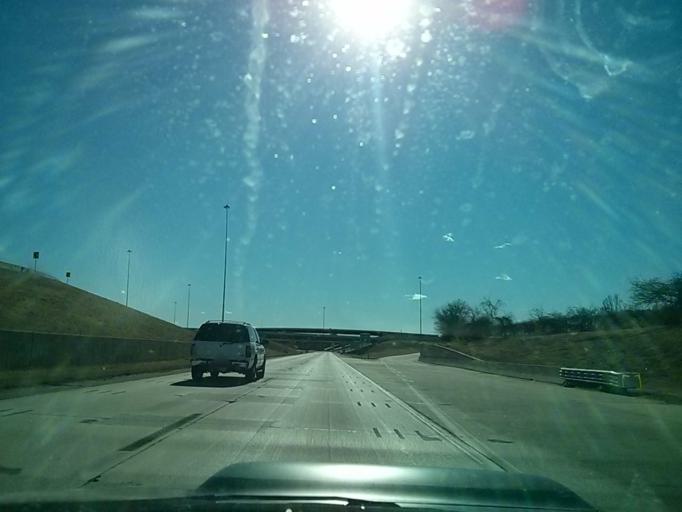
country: US
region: Oklahoma
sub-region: Tulsa County
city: Turley
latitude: 36.2027
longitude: -95.9484
